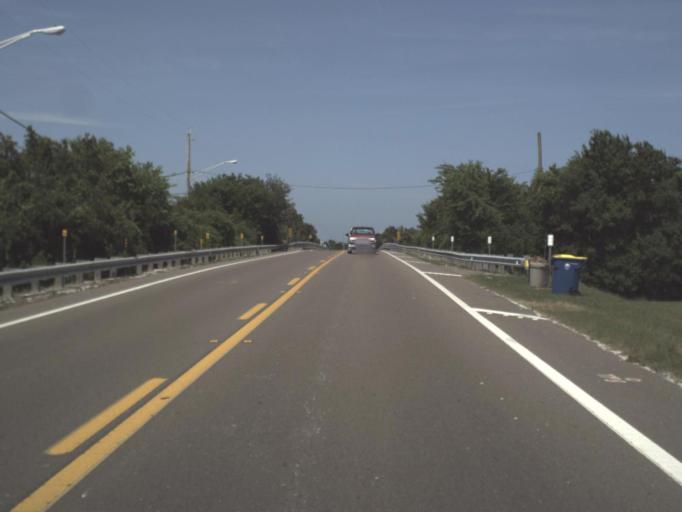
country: US
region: Florida
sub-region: Duval County
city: Atlantic Beach
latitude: 30.4077
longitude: -81.4263
